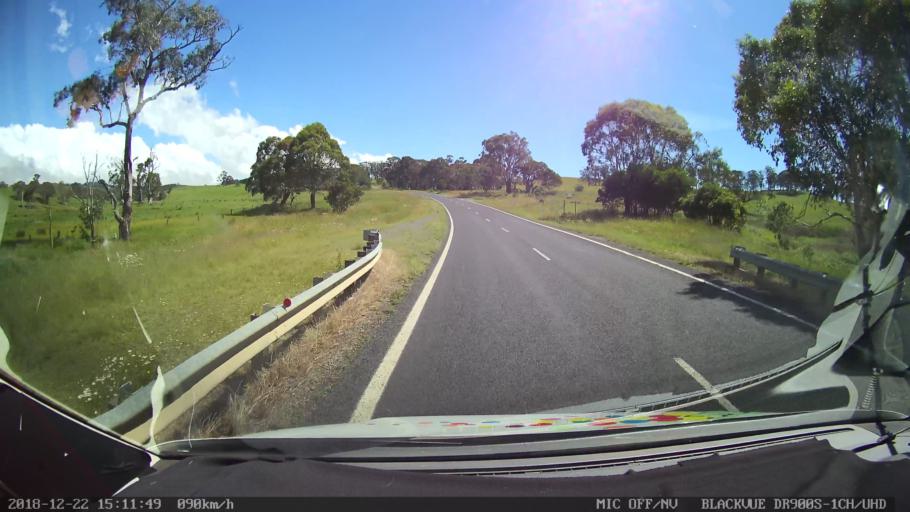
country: AU
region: New South Wales
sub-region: Bellingen
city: Dorrigo
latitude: -30.3481
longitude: 152.3989
